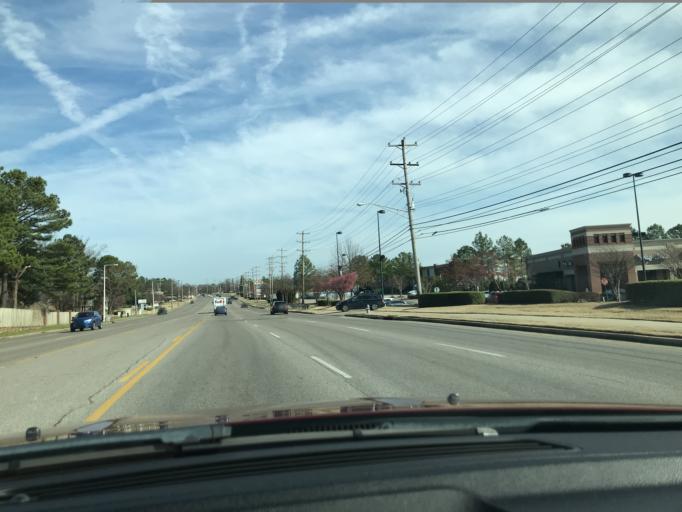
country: US
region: Tennessee
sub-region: Shelby County
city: Germantown
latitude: 35.0491
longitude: -89.8030
